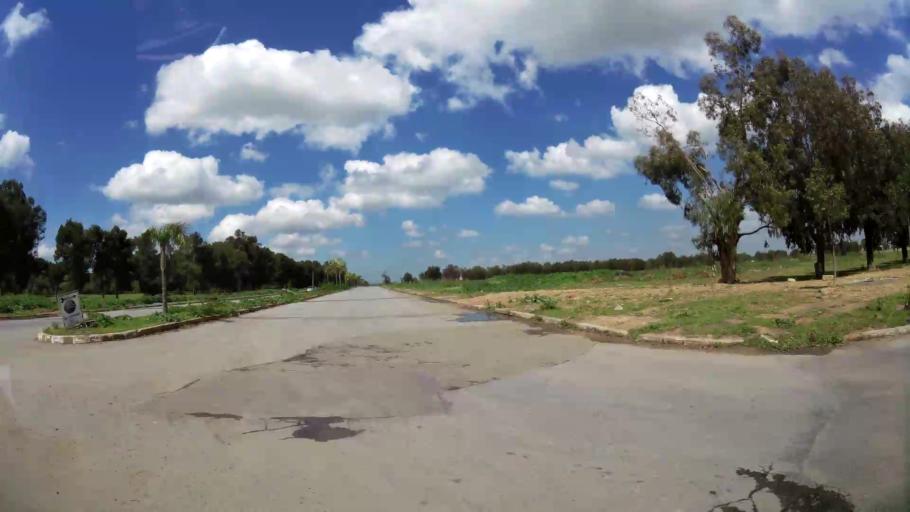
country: MA
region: Chaouia-Ouardigha
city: Nouaseur
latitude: 33.3740
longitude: -7.5543
